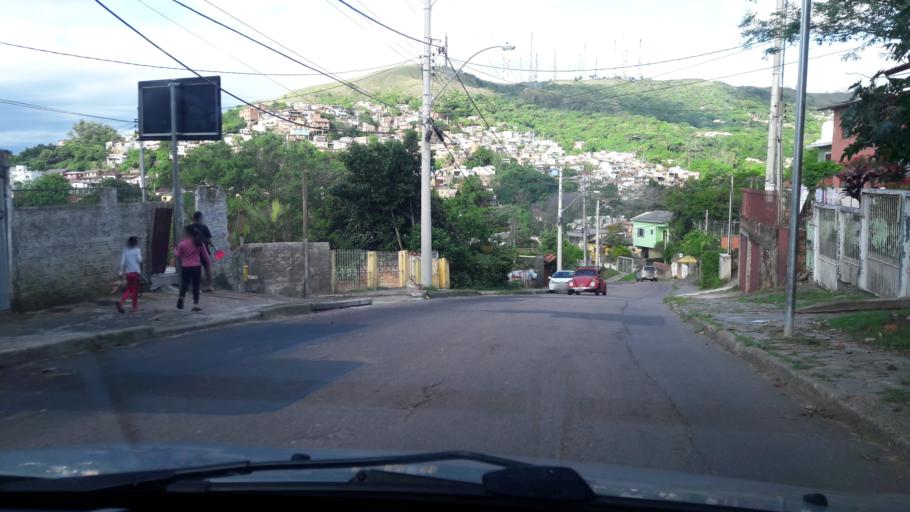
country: BR
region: Rio Grande do Sul
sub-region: Porto Alegre
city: Porto Alegre
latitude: -30.0843
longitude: -51.1990
